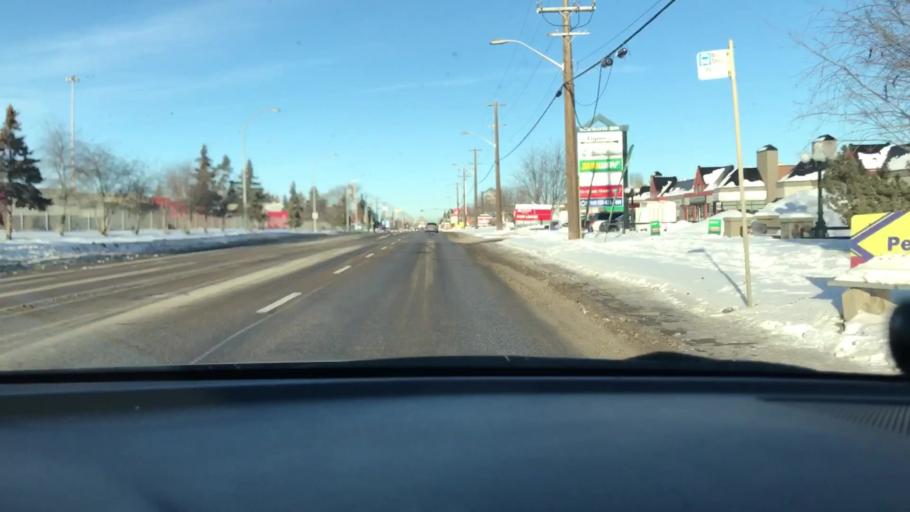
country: CA
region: Alberta
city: Edmonton
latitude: 53.4720
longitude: -113.4860
